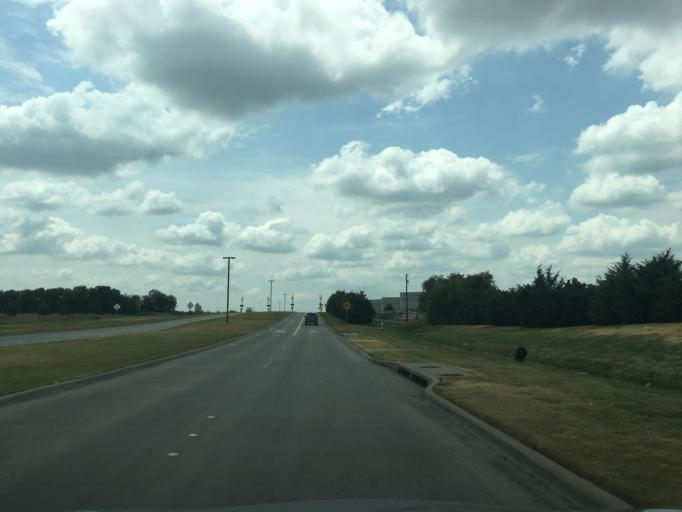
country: US
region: Texas
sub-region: Rockwall County
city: Rockwall
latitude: 32.9256
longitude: -96.4367
